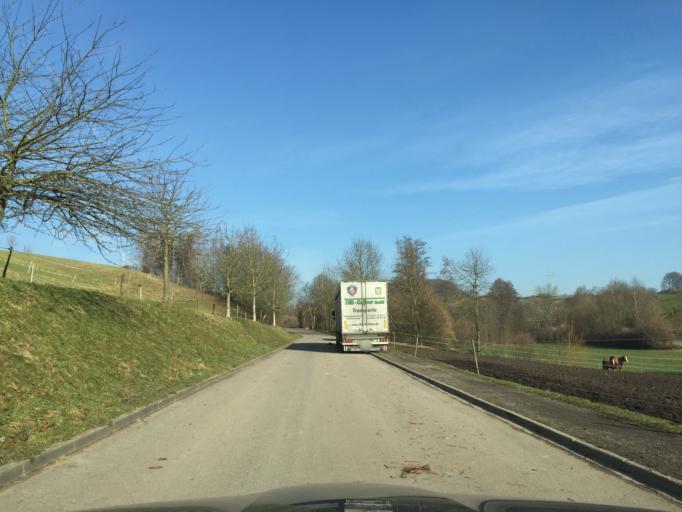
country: DE
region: Hesse
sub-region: Regierungsbezirk Darmstadt
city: Birkenau
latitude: 49.5710
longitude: 8.7025
